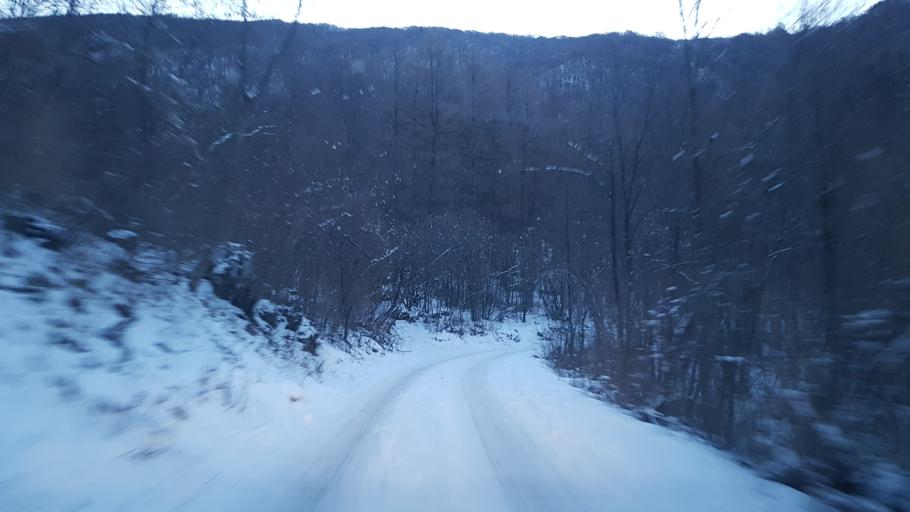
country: IT
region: Friuli Venezia Giulia
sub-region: Provincia di Udine
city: Montenars
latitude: 46.2779
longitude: 13.1598
